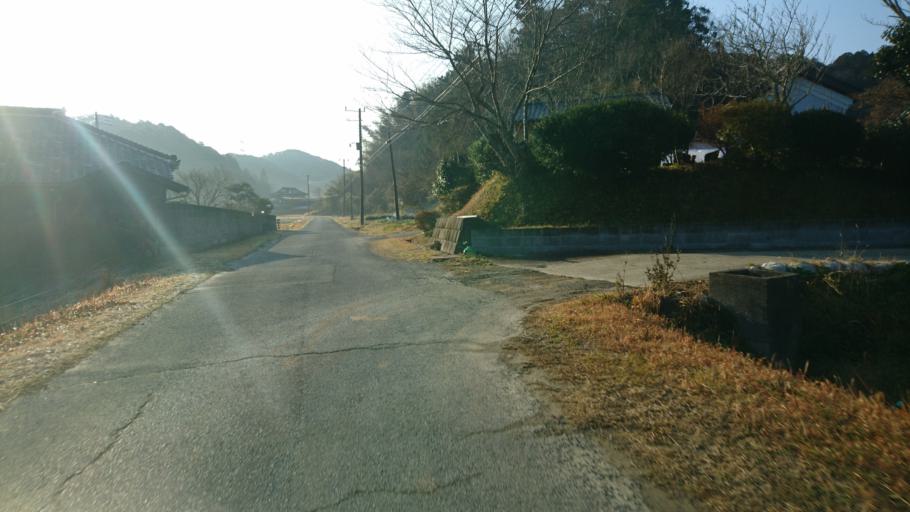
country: JP
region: Chiba
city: Kimitsu
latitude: 35.2920
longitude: 139.9512
